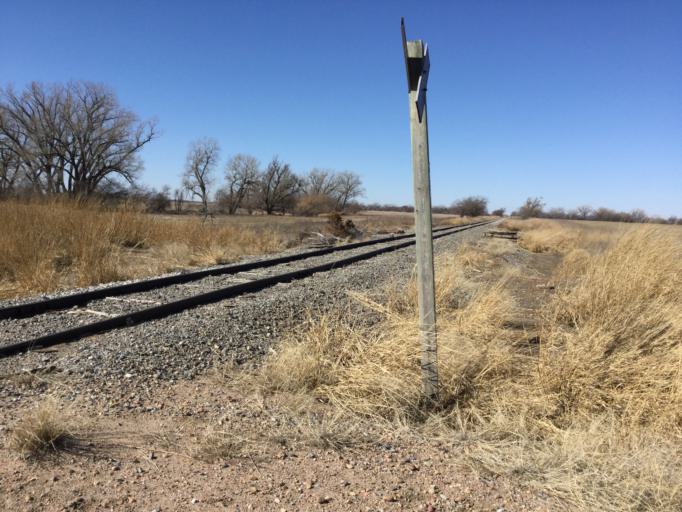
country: US
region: Kansas
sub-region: Pawnee County
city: Larned
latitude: 38.1631
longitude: -99.1548
